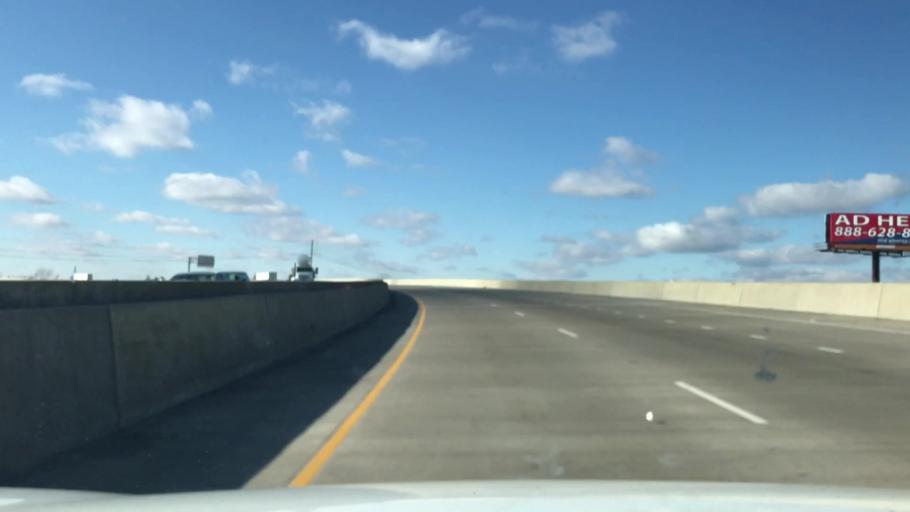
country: US
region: Illinois
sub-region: Madison County
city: Venice
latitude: 38.6487
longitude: -90.1612
